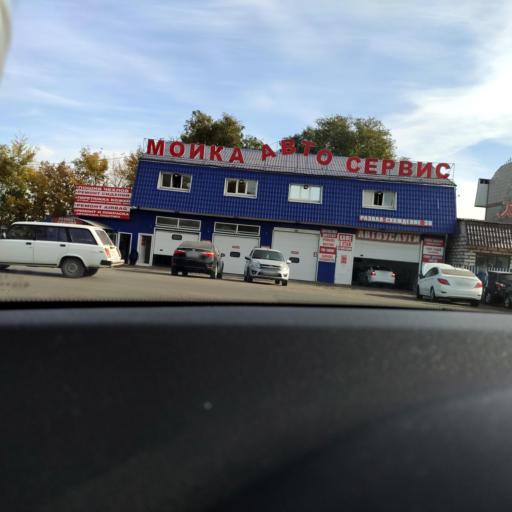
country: RU
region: Samara
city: Petra-Dubrava
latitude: 53.2459
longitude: 50.2696
